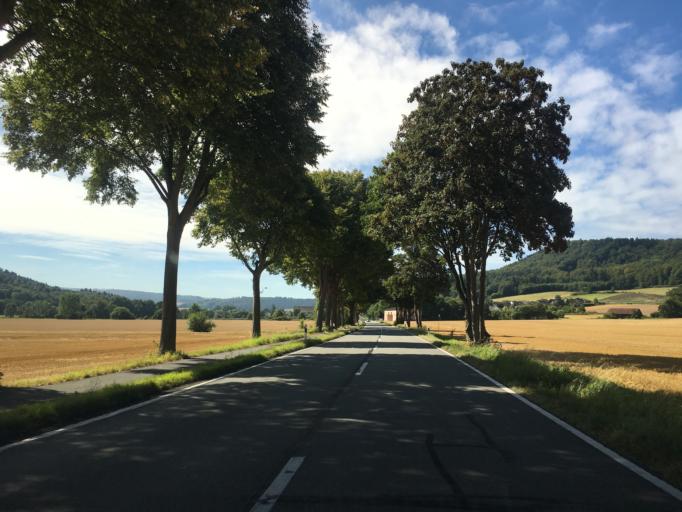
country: DE
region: Lower Saxony
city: Hameln
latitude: 52.0354
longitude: 9.3506
